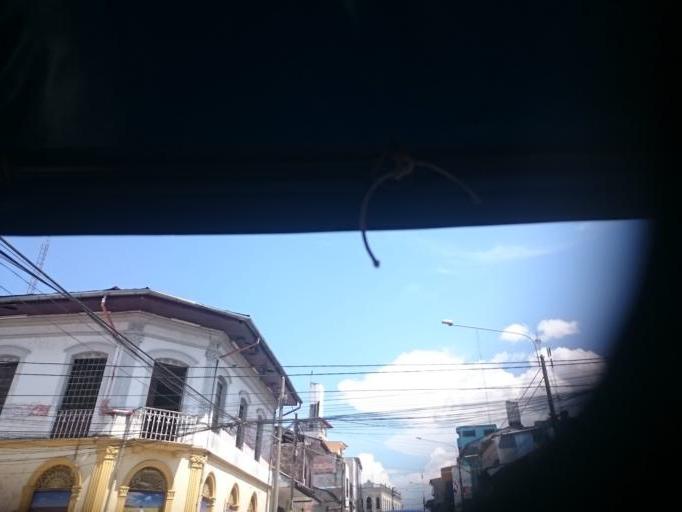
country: PE
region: Loreto
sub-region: Provincia de Maynas
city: Iquitos
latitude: -3.7476
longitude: -73.2424
